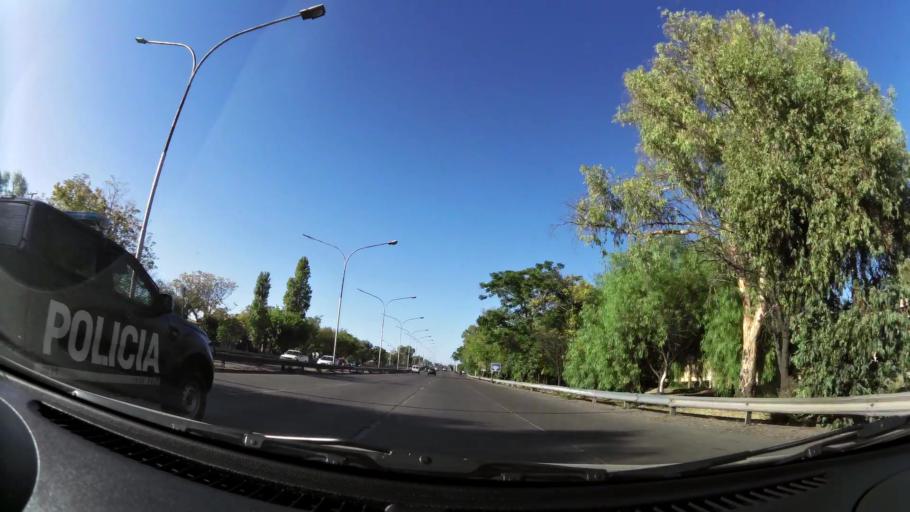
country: AR
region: Mendoza
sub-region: Departamento de Godoy Cruz
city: Godoy Cruz
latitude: -32.9154
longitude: -68.8374
